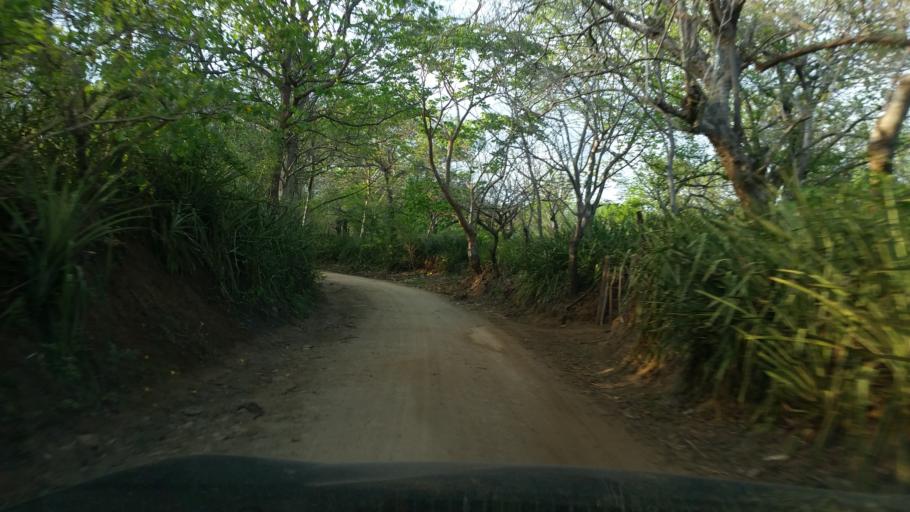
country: NI
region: Managua
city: Masachapa
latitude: 11.7950
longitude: -86.4699
